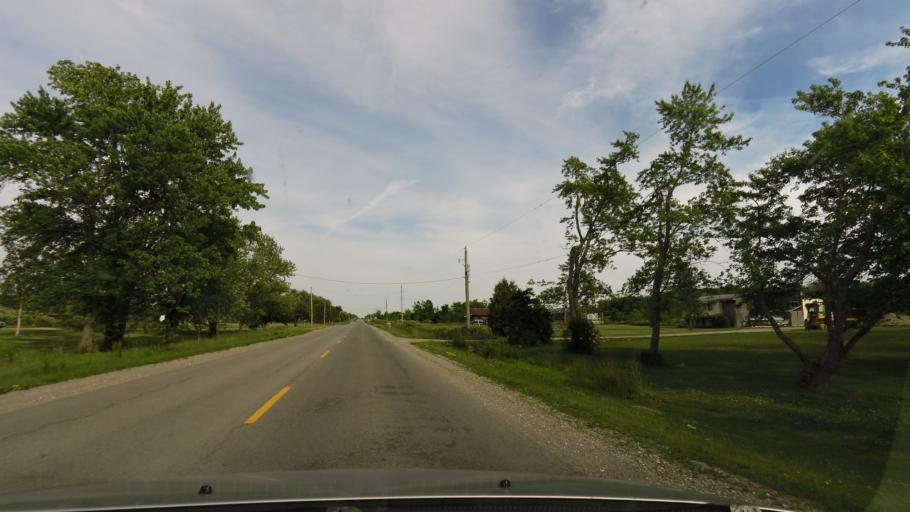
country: CA
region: Ontario
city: Ancaster
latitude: 43.0348
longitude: -80.0258
